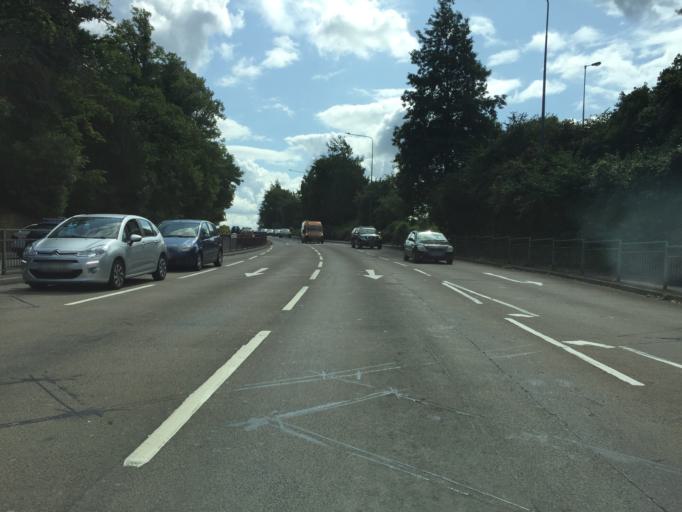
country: GB
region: England
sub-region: Kent
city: Aylesford
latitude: 51.2939
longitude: 0.4722
